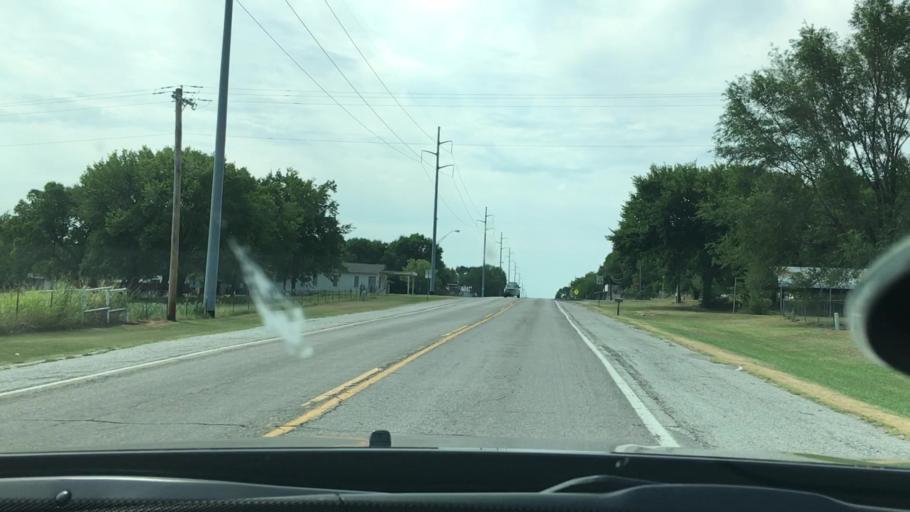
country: US
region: Oklahoma
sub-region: Carter County
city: Ardmore
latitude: 34.3168
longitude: -97.1430
